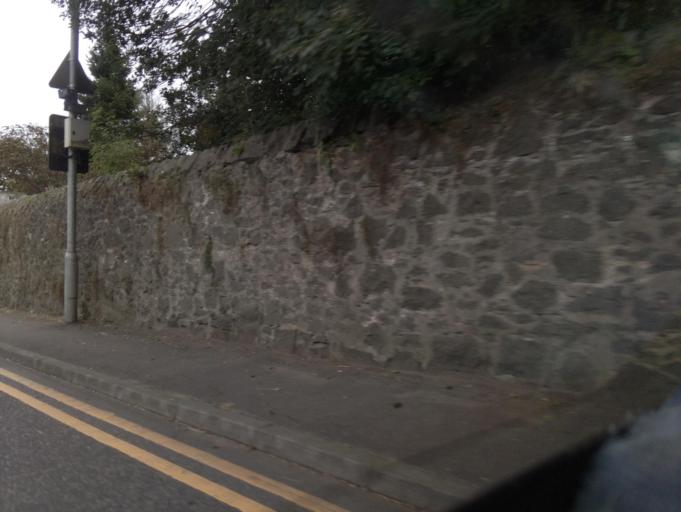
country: GB
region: Scotland
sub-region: Fife
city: Leslie
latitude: 56.2022
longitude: -3.2181
